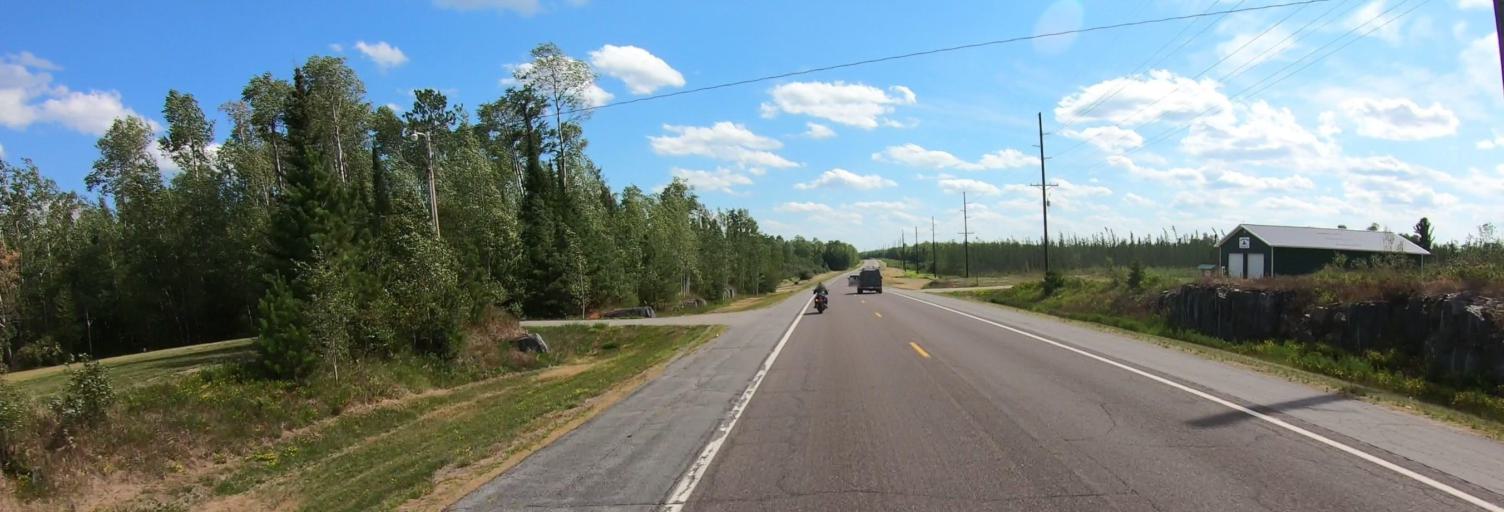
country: US
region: Minnesota
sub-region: Saint Louis County
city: Aurora
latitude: 47.8346
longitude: -92.3723
